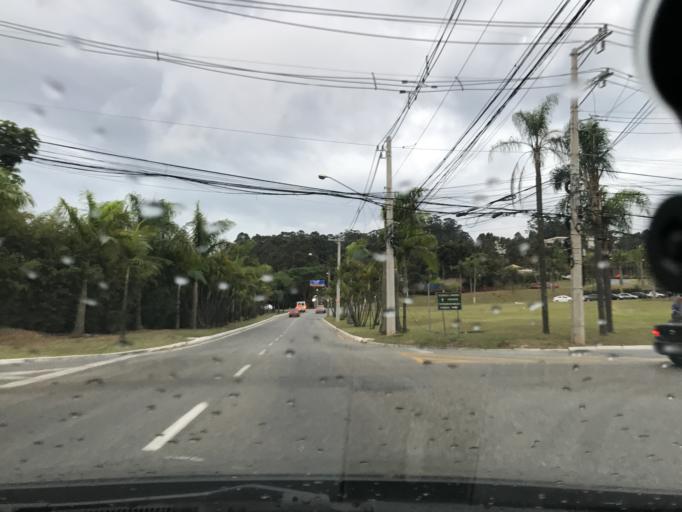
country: BR
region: Sao Paulo
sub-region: Carapicuiba
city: Carapicuiba
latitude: -23.4970
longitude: -46.8301
